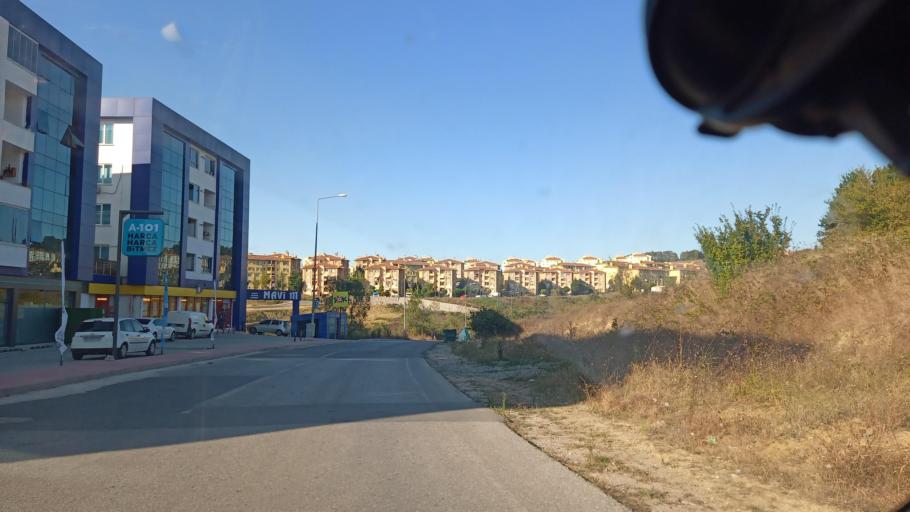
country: TR
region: Kocaeli
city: Kaymaz
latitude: 40.8581
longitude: 30.2772
